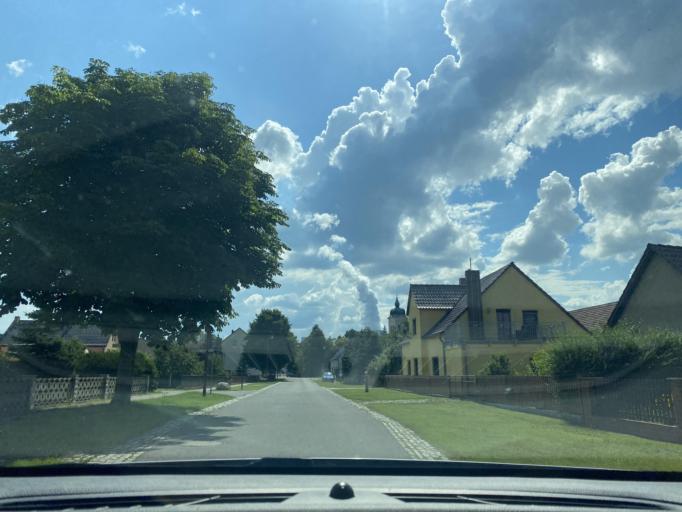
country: DE
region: Saxony
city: Boxberg
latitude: 51.4328
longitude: 14.6016
